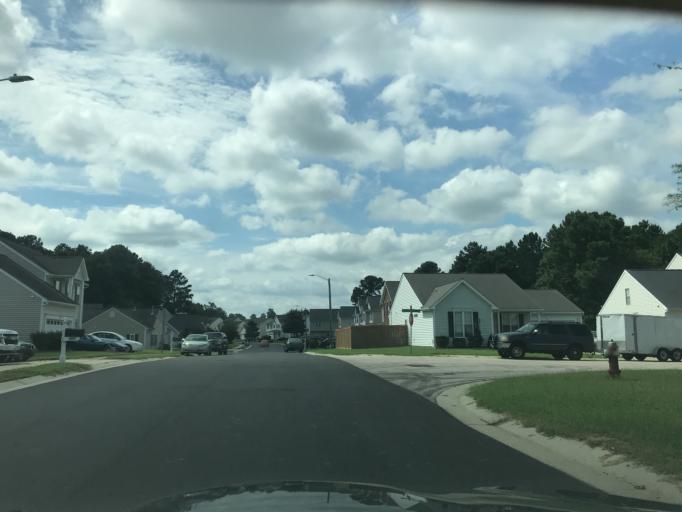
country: US
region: North Carolina
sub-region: Wake County
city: Rolesville
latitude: 35.8931
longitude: -78.5454
